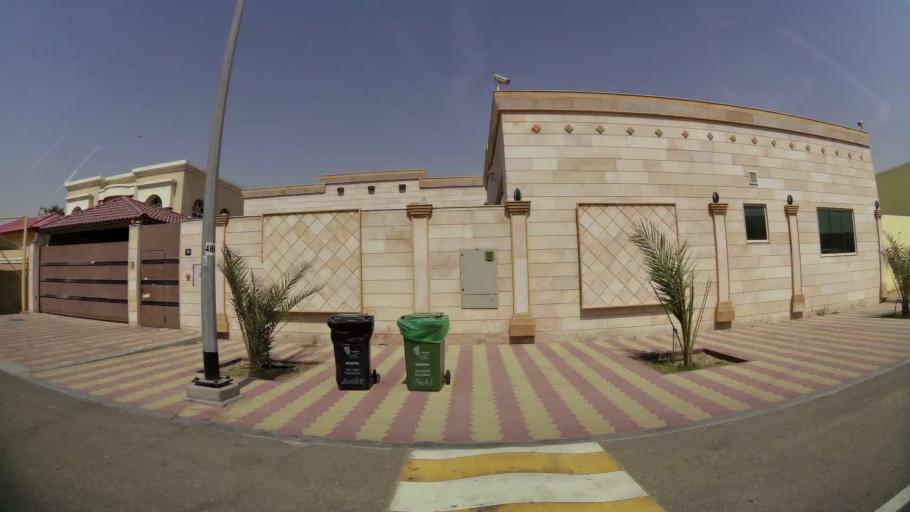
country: AE
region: Ash Shariqah
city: Sharjah
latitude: 25.2343
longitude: 55.4476
